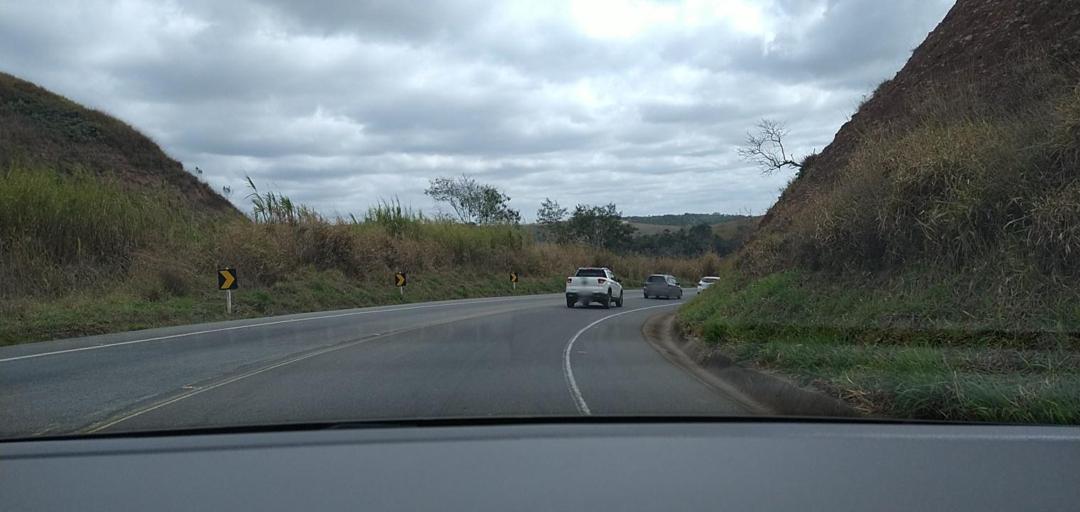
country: BR
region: Minas Gerais
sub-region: Ponte Nova
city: Ponte Nova
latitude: -20.5296
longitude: -42.8946
